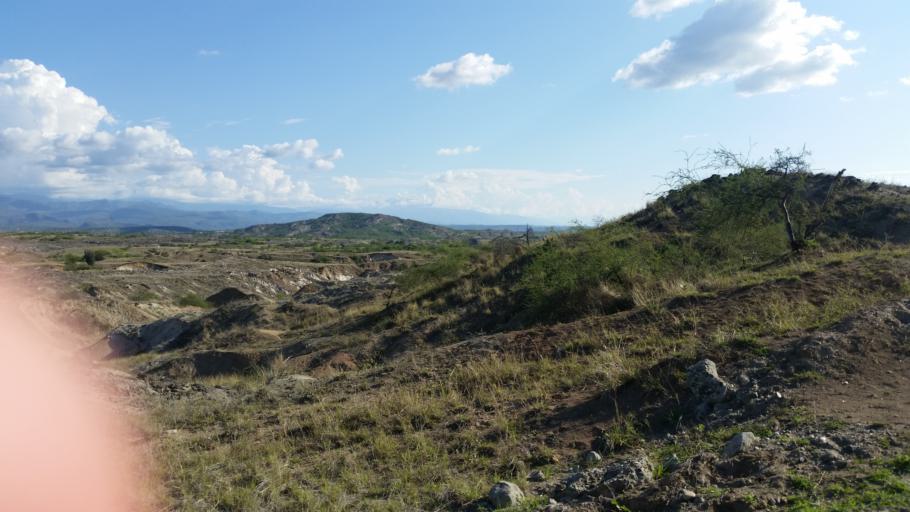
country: CO
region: Huila
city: Baraya
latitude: 3.2362
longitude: -75.1022
